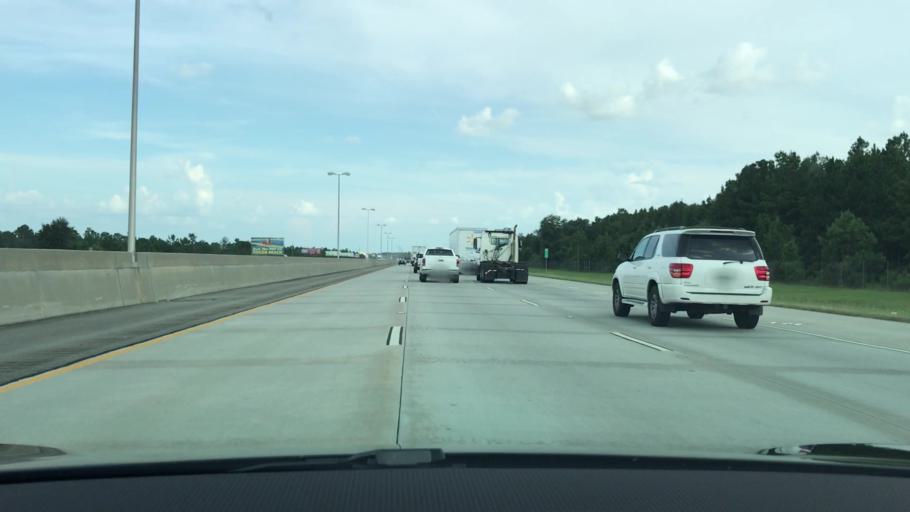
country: US
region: Georgia
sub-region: Cook County
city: Adel
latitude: 31.0804
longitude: -83.4119
